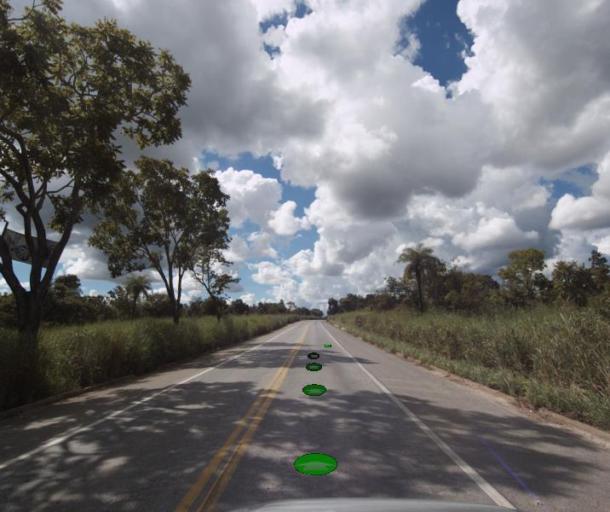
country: BR
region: Goias
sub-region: Porangatu
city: Porangatu
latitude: -13.4129
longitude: -49.1316
